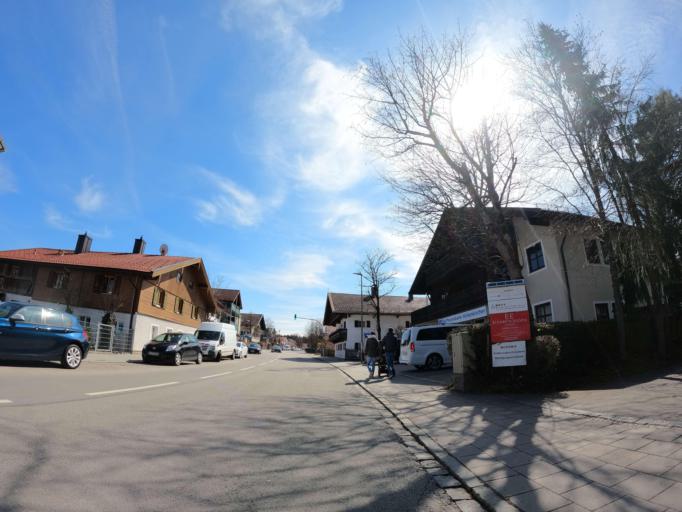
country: DE
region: Bavaria
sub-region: Upper Bavaria
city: Hohenkirchen-Siegertsbrunn
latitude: 48.0172
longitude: 11.7123
